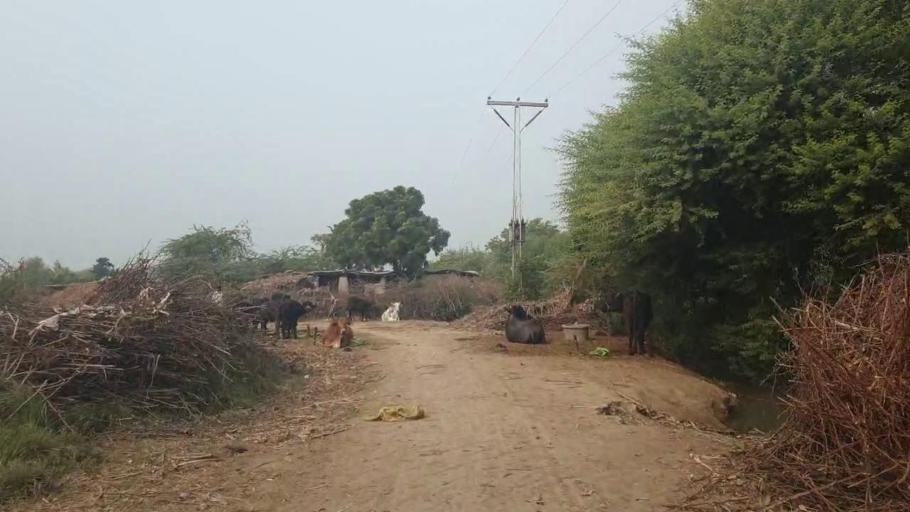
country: PK
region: Sindh
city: Tando Adam
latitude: 25.7168
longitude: 68.6154
